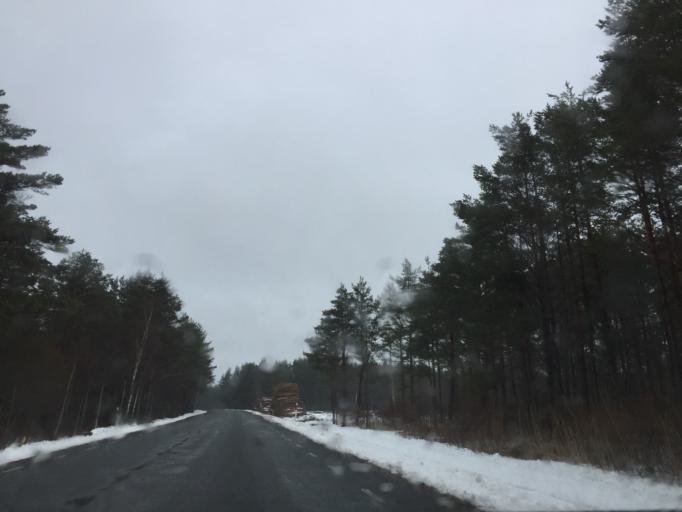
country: EE
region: Saare
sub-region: Kuressaare linn
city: Kuressaare
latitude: 58.3088
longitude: 22.0245
